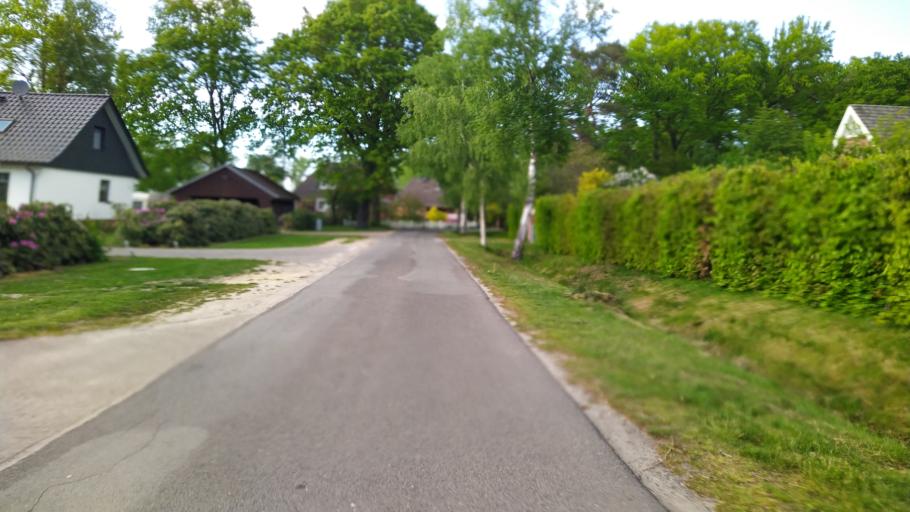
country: DE
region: Lower Saxony
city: Farven
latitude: 53.4321
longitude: 9.3501
